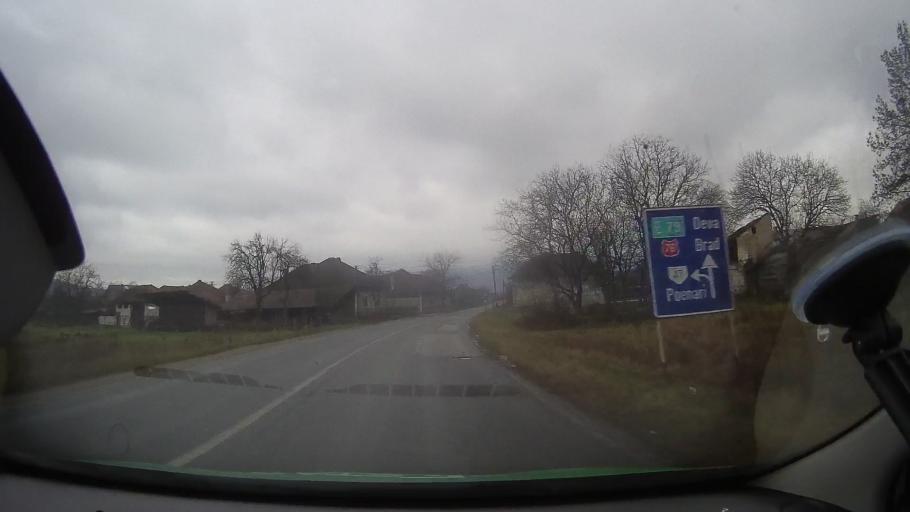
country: RO
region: Arad
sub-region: Comuna Halmagiu
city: Halmagiu
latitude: 46.2653
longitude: 22.5965
